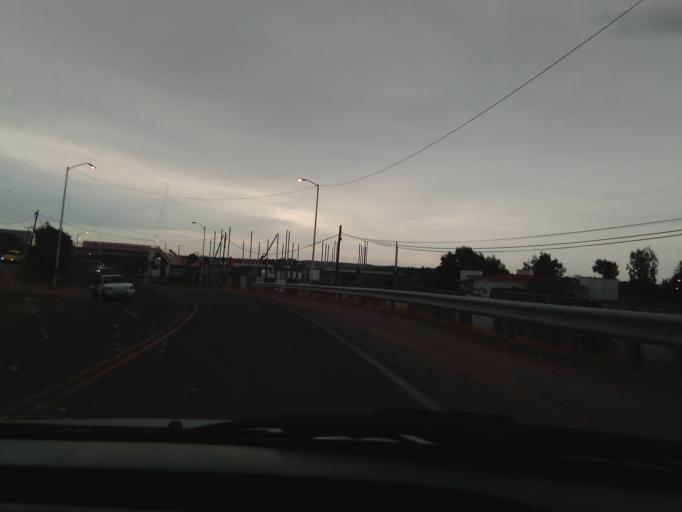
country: MX
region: Guanajuato
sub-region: Dolores Hidalgo Cuna de la Independencia Nacional
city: Ejido Jesus Maria
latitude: 21.1637
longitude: -100.9026
